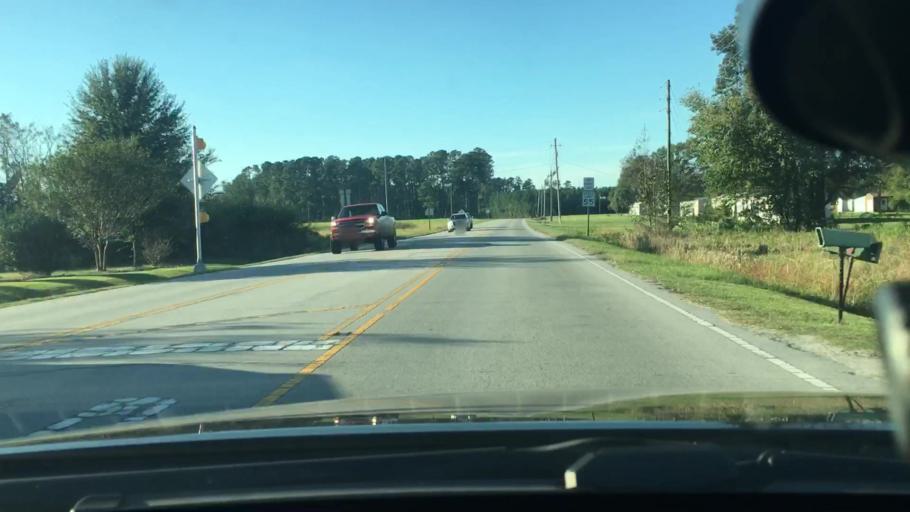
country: US
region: North Carolina
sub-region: Pitt County
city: Windsor
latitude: 35.4651
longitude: -77.2757
